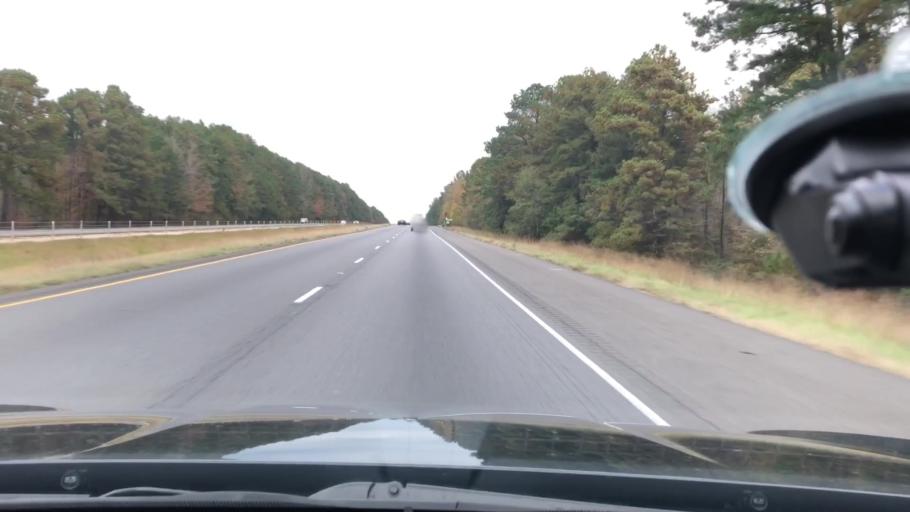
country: US
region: Arkansas
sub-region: Clark County
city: Arkadelphia
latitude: 34.2693
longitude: -92.9724
